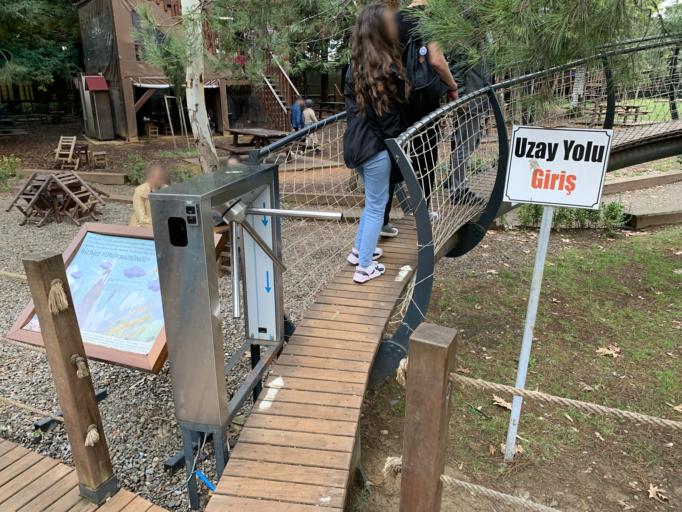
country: TR
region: Trabzon
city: Trabzon
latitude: 40.9975
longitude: 39.6757
